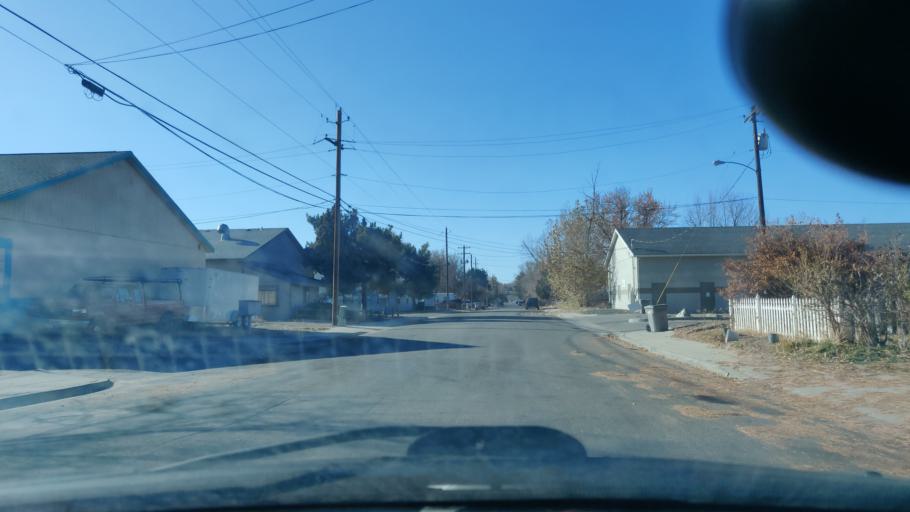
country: US
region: Idaho
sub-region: Ada County
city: Garden City
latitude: 43.6392
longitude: -116.2476
